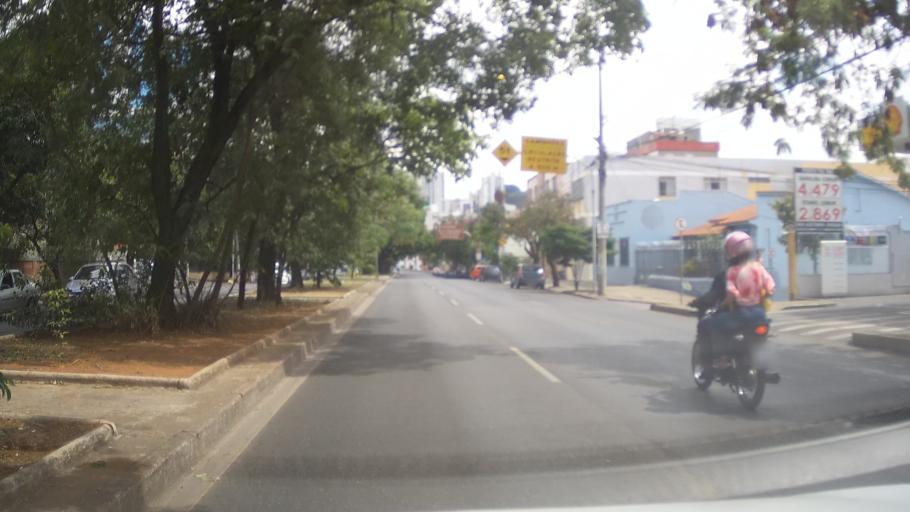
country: BR
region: Minas Gerais
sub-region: Belo Horizonte
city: Belo Horizonte
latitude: -19.9242
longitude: -43.9580
